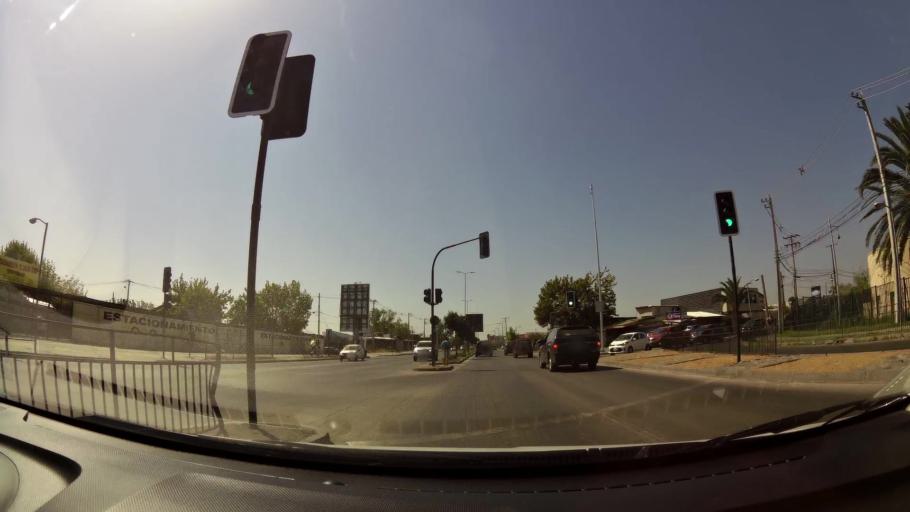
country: CL
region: Maule
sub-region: Provincia de Talca
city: Talca
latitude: -35.4257
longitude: -71.6452
